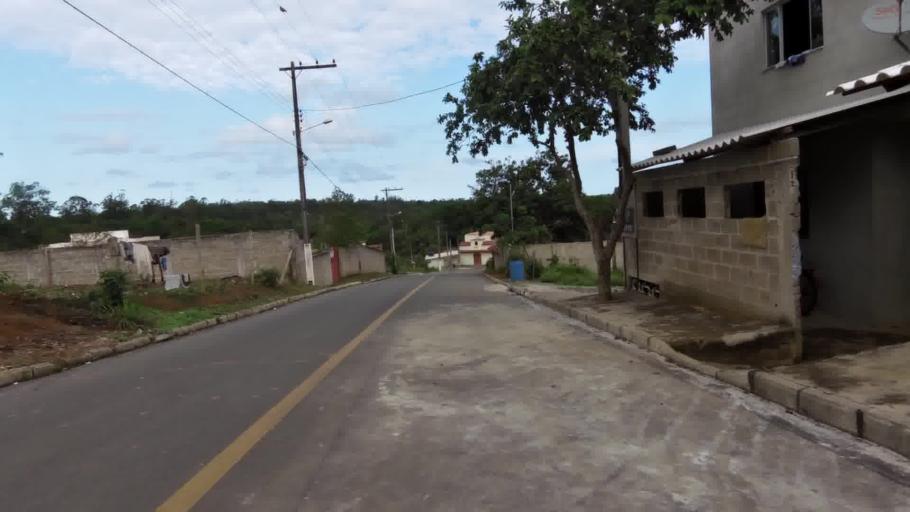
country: BR
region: Espirito Santo
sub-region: Piuma
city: Piuma
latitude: -20.7935
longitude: -40.6404
